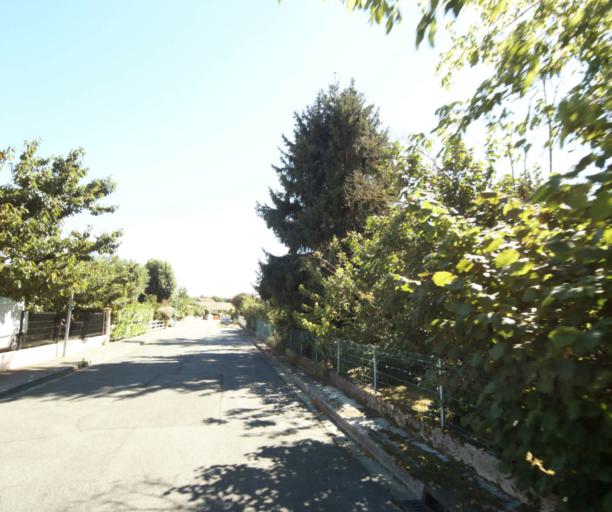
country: FR
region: Midi-Pyrenees
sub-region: Departement de la Haute-Garonne
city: Castanet-Tolosan
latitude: 43.5234
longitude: 1.4989
